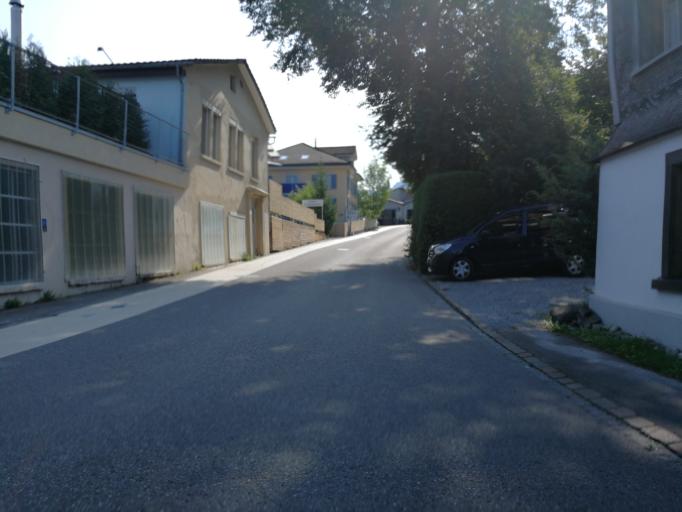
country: CH
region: Saint Gallen
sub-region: Wahlkreis Toggenburg
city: Ebnat-Kappel
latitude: 47.2583
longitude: 9.1280
